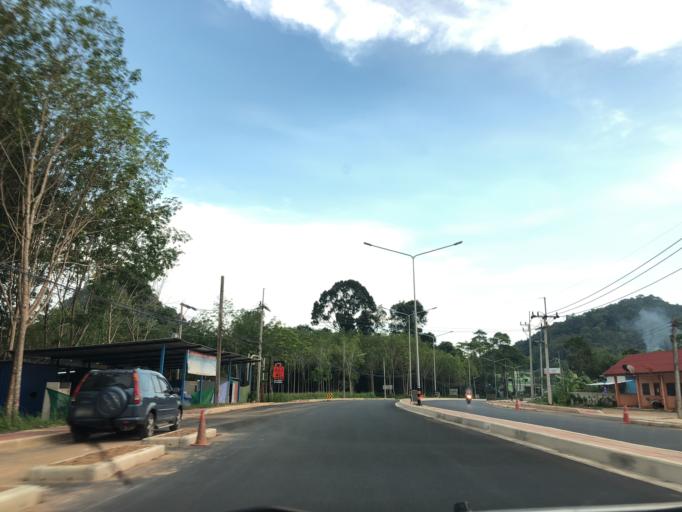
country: TH
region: Phangnga
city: Ban Ao Nang
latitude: 8.0583
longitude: 98.8403
